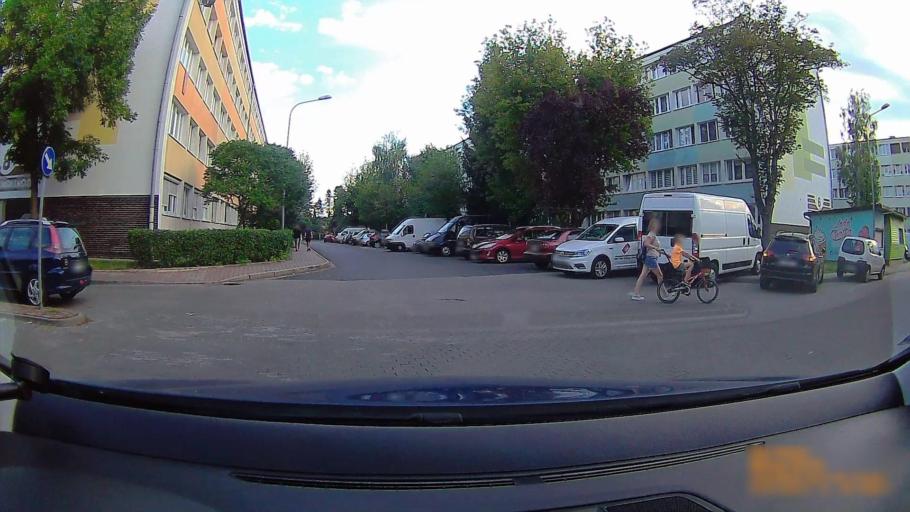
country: PL
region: Greater Poland Voivodeship
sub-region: Konin
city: Konin
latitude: 52.2285
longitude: 18.2665
